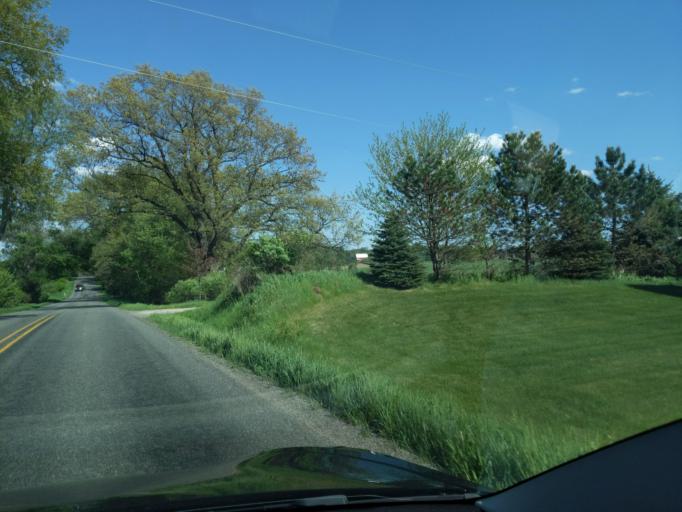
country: US
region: Michigan
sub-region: Barry County
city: Middleville
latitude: 42.7981
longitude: -85.4002
